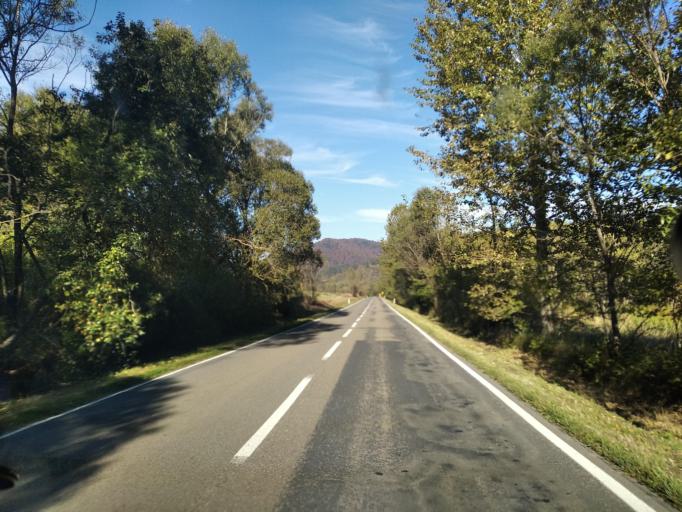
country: PL
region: Subcarpathian Voivodeship
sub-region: Powiat leski
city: Cisna
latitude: 49.2558
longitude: 22.2861
